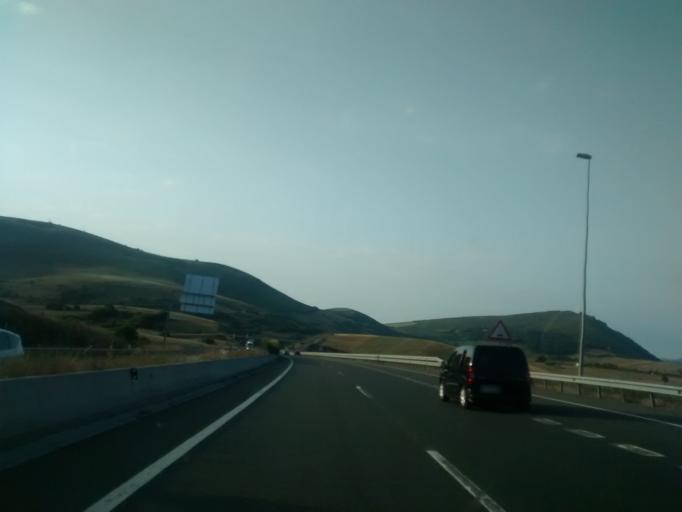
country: ES
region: Cantabria
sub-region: Provincia de Cantabria
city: Santiurde de Reinosa
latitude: 43.0722
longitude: -4.0857
